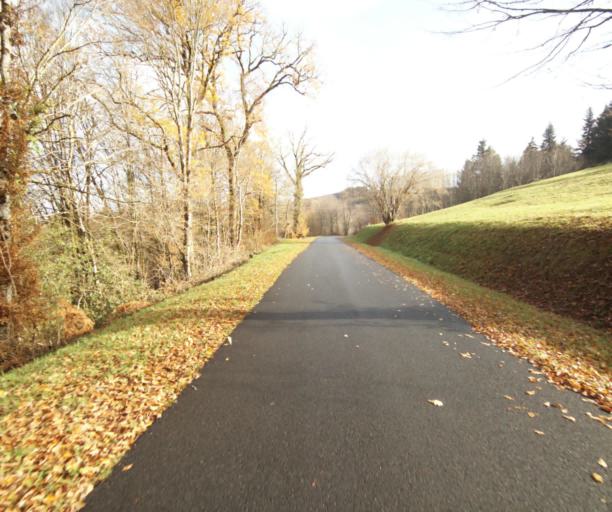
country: FR
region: Limousin
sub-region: Departement de la Correze
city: Cornil
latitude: 45.2150
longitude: 1.6915
